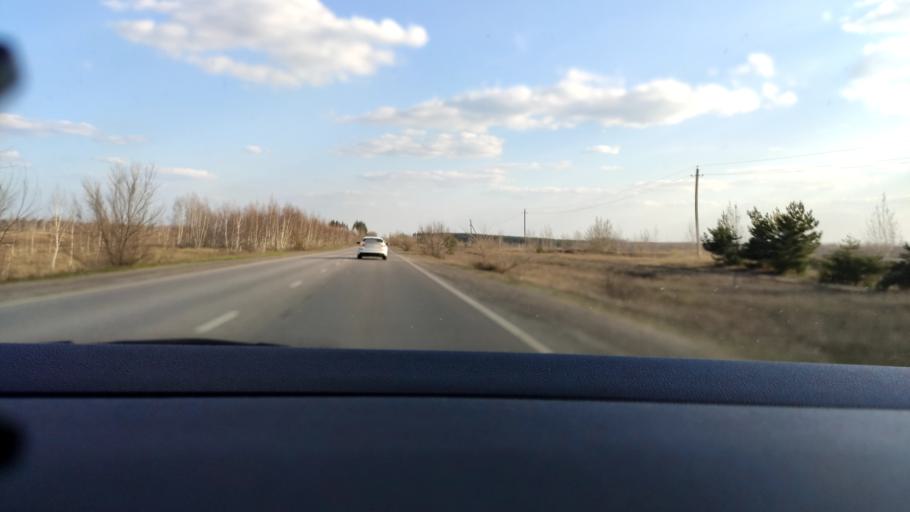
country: RU
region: Voronezj
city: Maslovka
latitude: 51.5745
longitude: 39.2680
